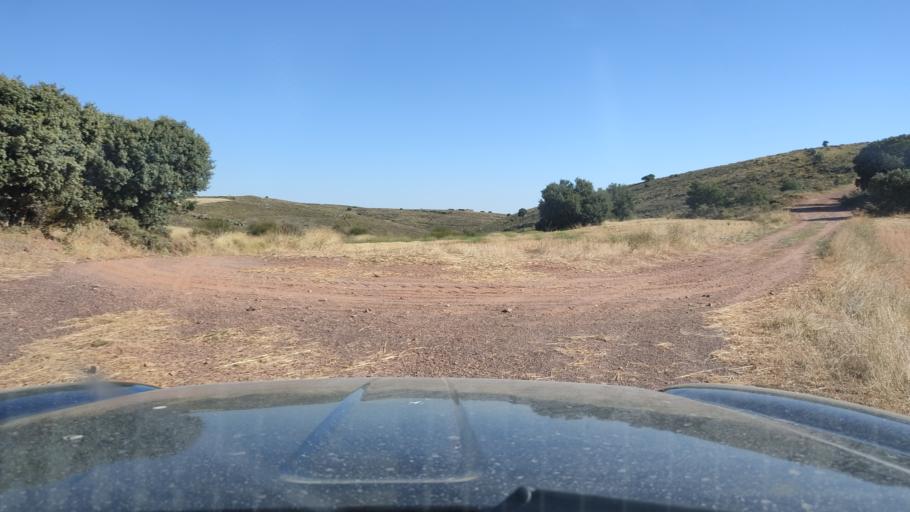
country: ES
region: Aragon
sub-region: Provincia de Teruel
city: Monforte de Moyuela
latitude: 41.0252
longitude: -1.0078
